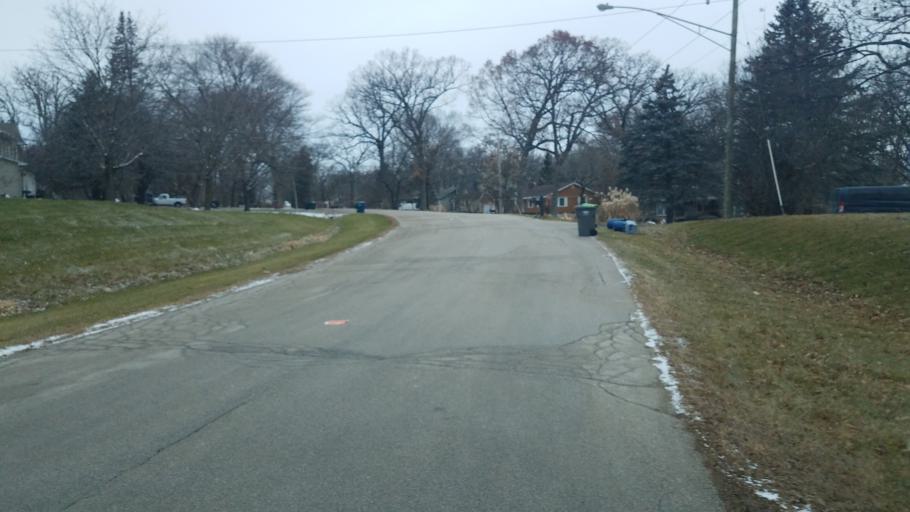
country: US
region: Illinois
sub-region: Kane County
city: Elburn
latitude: 41.8283
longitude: -88.4663
